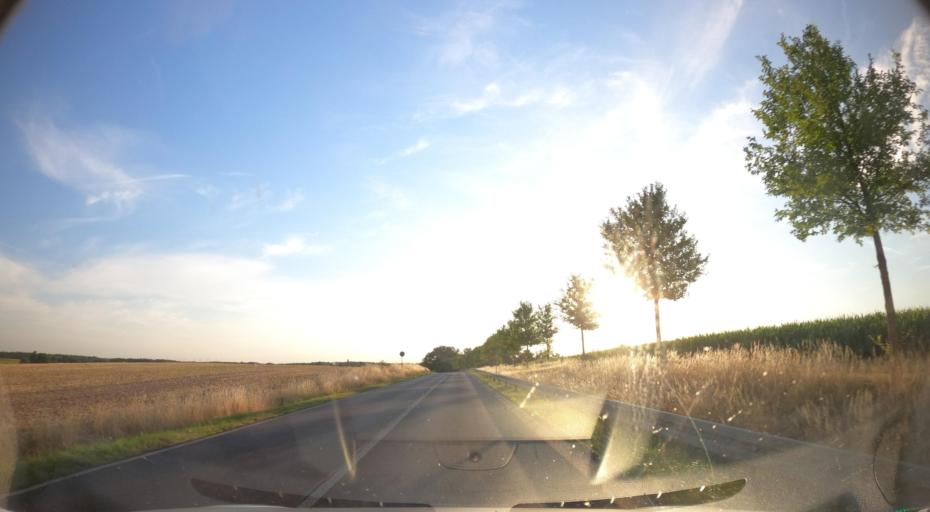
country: PL
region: West Pomeranian Voivodeship
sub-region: Powiat policki
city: Dobra
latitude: 53.4558
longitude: 14.2871
